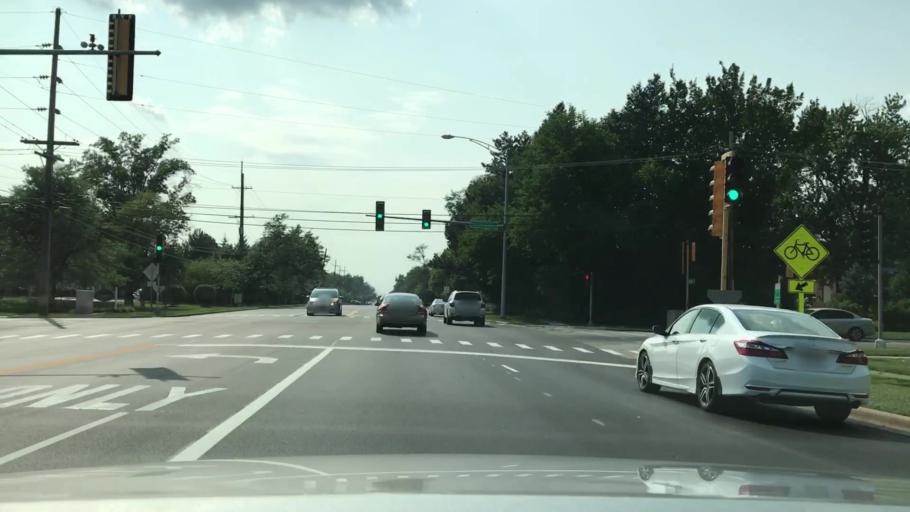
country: US
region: Illinois
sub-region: DuPage County
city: Willowbrook
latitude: 41.7741
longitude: -87.9548
